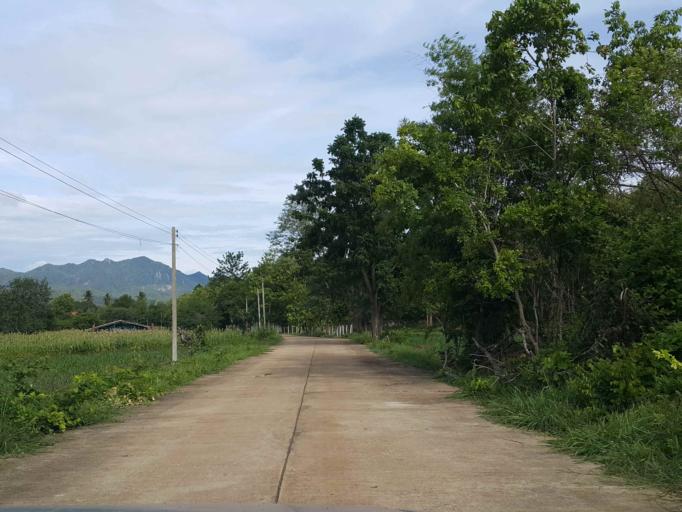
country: TH
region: Sukhothai
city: Thung Saliam
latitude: 17.2268
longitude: 99.5296
